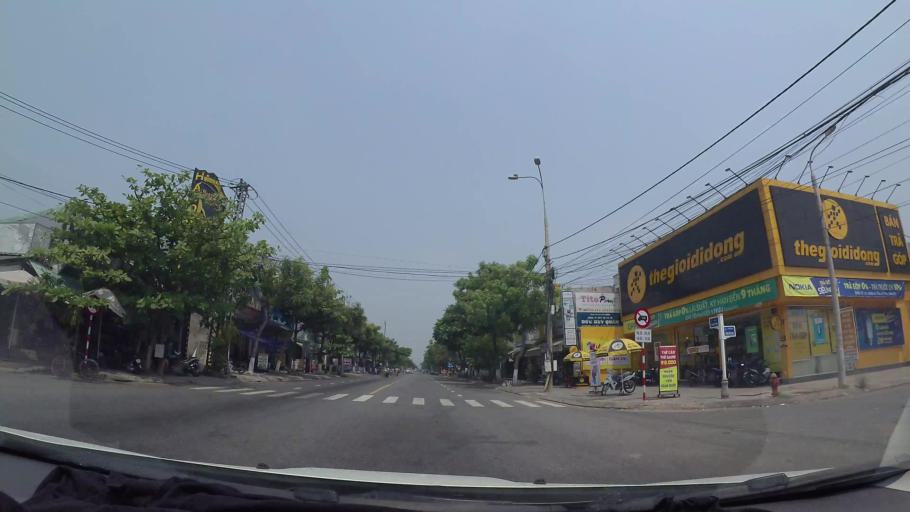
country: VN
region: Da Nang
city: Cam Le
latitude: 15.9827
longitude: 108.2081
